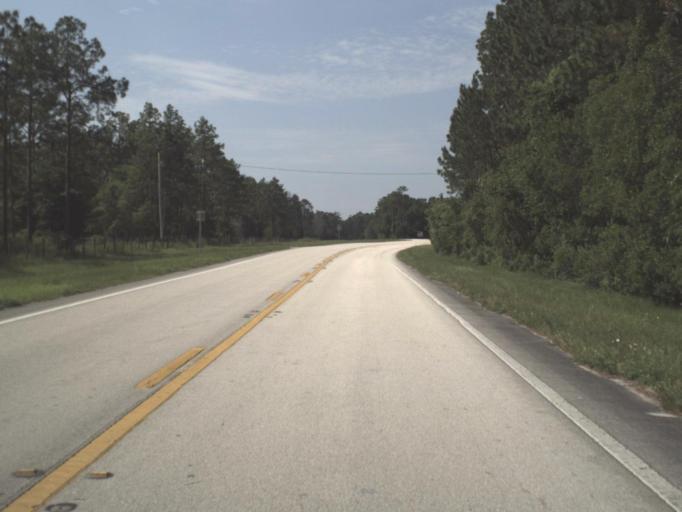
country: US
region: Florida
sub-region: Bradford County
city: Starke
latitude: 29.9454
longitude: -82.0163
